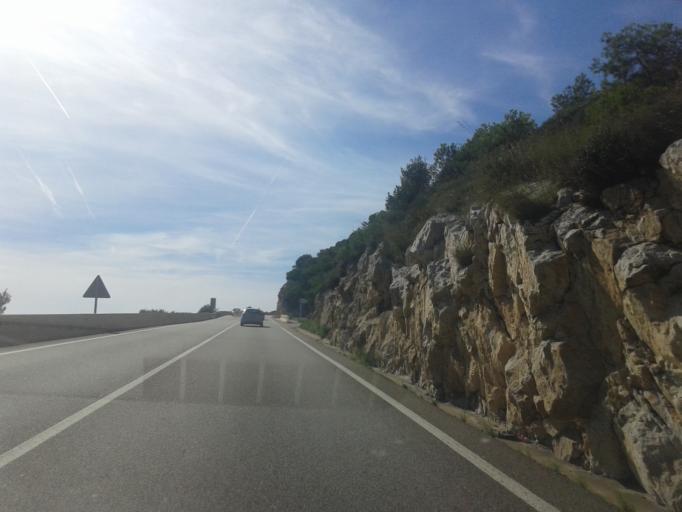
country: ES
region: Catalonia
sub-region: Provincia de Barcelona
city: Castelldefels
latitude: 41.2592
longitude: 1.9191
